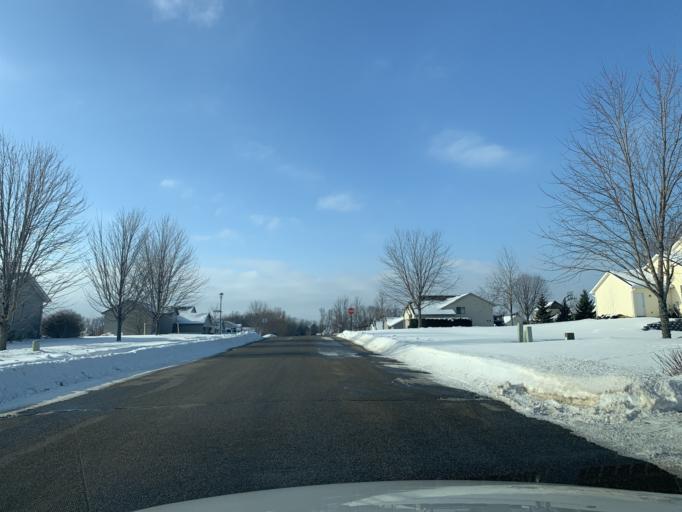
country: US
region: Minnesota
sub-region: Wright County
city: Buffalo
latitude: 45.2009
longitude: -93.8332
